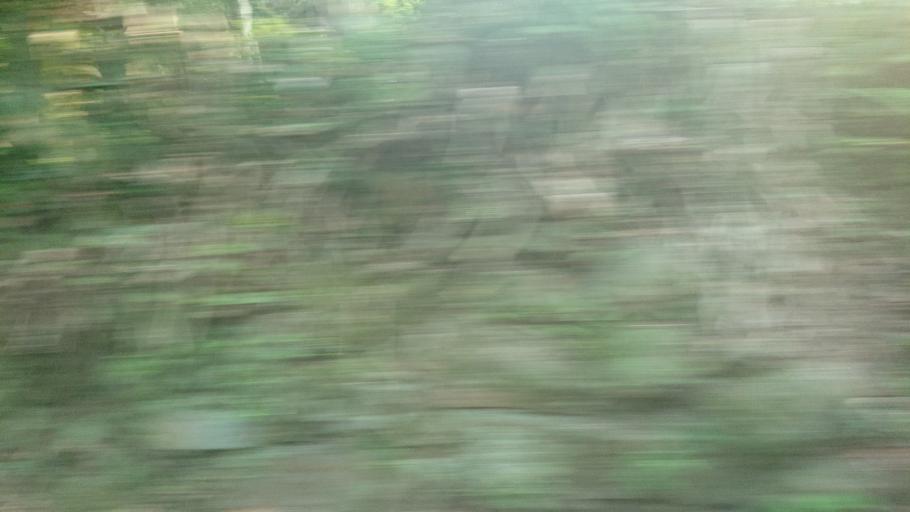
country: TW
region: Taiwan
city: Daxi
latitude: 24.8686
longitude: 121.4148
